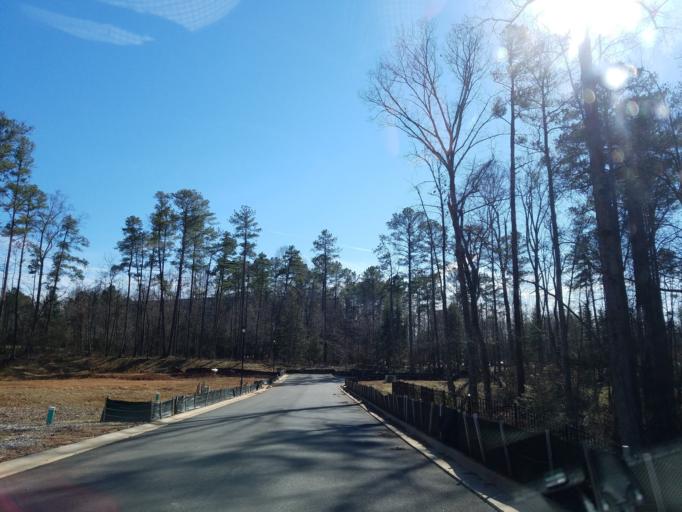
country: US
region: Georgia
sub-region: Fulton County
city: Alpharetta
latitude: 34.0508
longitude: -84.3126
